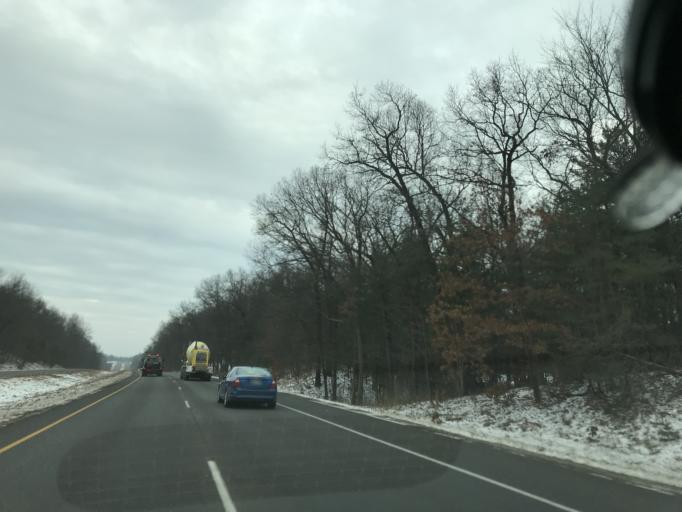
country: US
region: Michigan
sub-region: Kent County
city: Rockford
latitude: 43.1094
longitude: -85.5503
